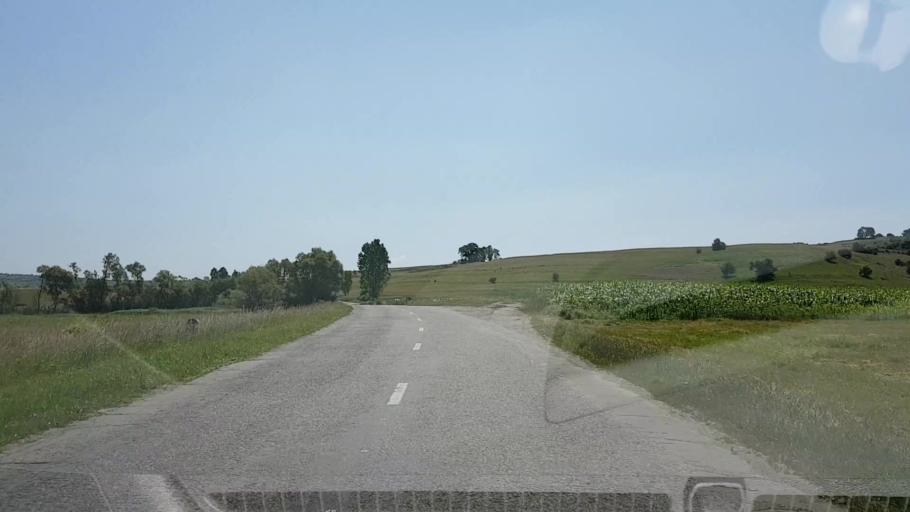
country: RO
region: Sibiu
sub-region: Comuna Merghindeal
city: Merghindeal
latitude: 45.9578
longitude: 24.7619
